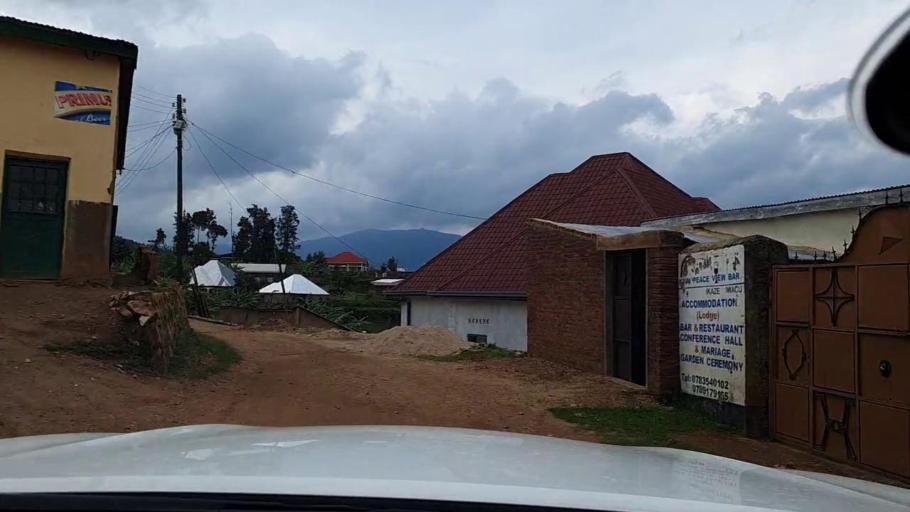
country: RW
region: Western Province
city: Kibuye
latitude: -2.1856
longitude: 29.2932
